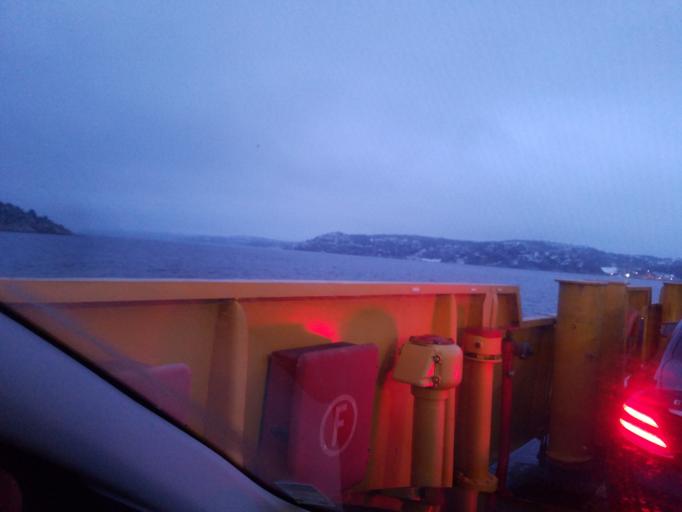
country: SE
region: Vaestra Goetaland
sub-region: Lysekils Kommun
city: Lysekil
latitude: 58.3015
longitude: 11.5124
